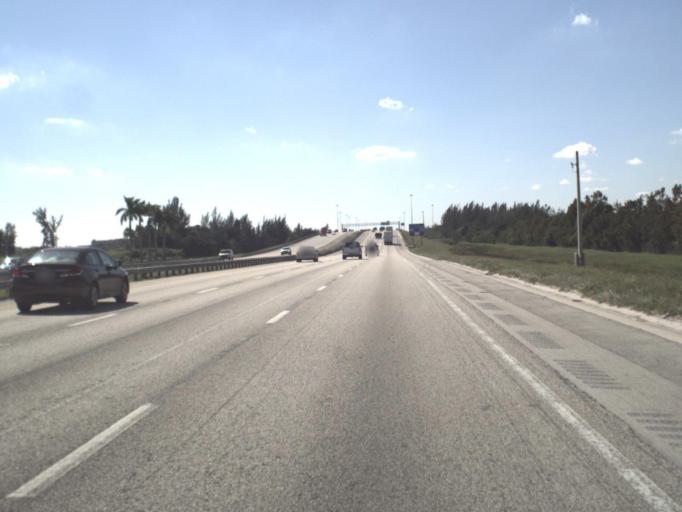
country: US
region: Florida
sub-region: Miami-Dade County
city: Hialeah Gardens
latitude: 25.8830
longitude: -80.3887
